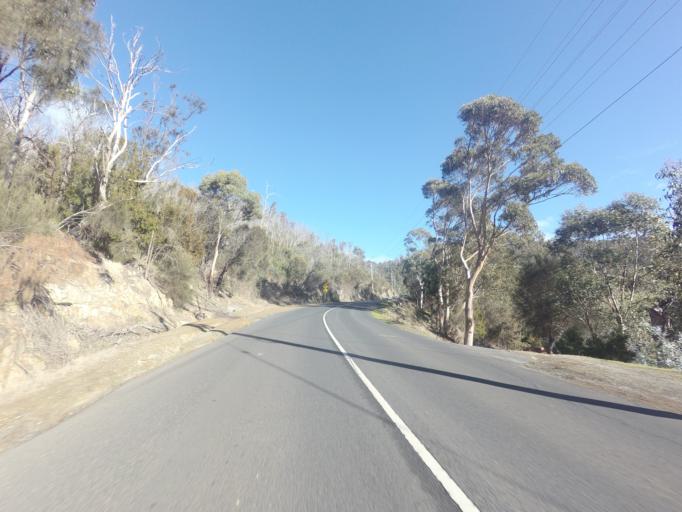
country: AU
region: Tasmania
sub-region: Glenorchy
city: Berriedale
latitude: -42.8203
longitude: 147.2145
